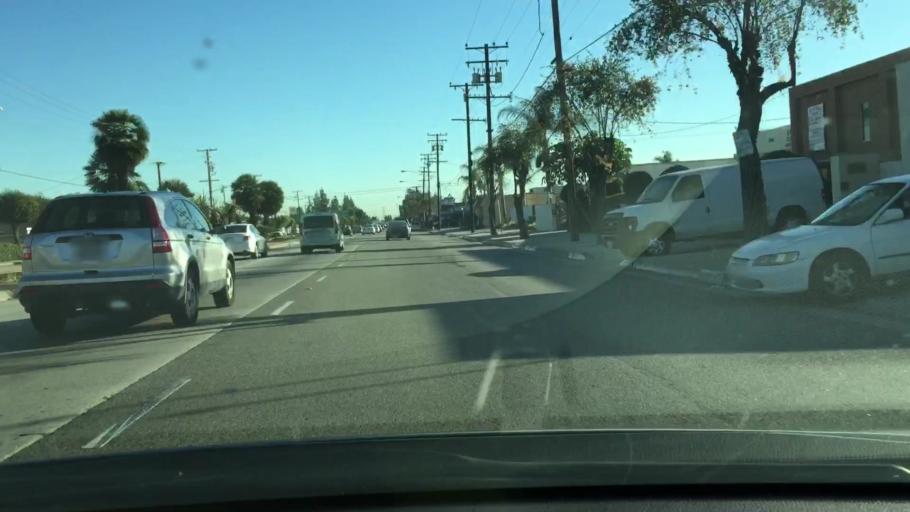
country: US
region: California
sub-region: Los Angeles County
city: South El Monte
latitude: 34.0567
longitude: -118.0645
